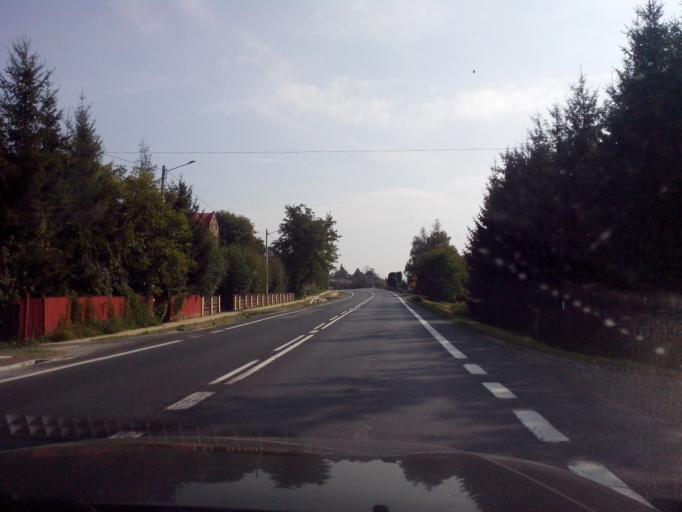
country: PL
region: Subcarpathian Voivodeship
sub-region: Powiat strzyzowski
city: Babica
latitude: 49.9365
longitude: 21.8818
